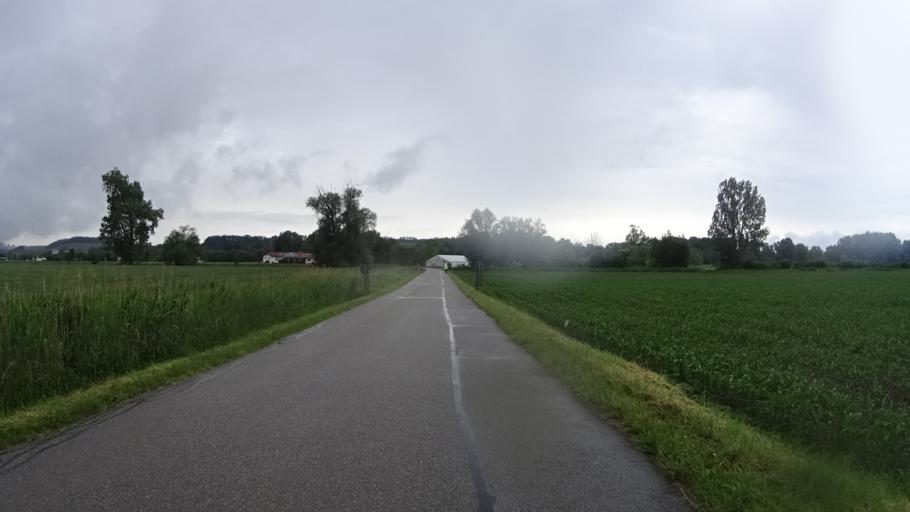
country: DE
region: Bavaria
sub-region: Lower Bavaria
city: Pocking
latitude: 48.4076
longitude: 13.2882
